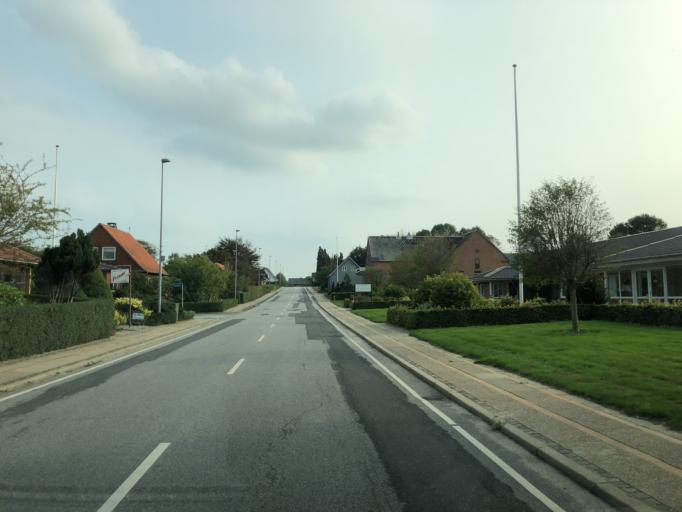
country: DK
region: Central Jutland
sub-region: Ringkobing-Skjern Kommune
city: Videbaek
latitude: 56.0879
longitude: 8.7024
